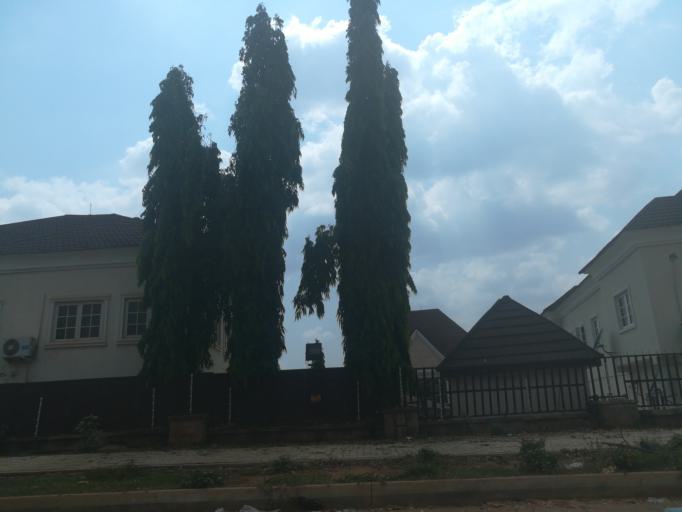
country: NG
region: Abuja Federal Capital Territory
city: Abuja
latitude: 9.0590
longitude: 7.4502
